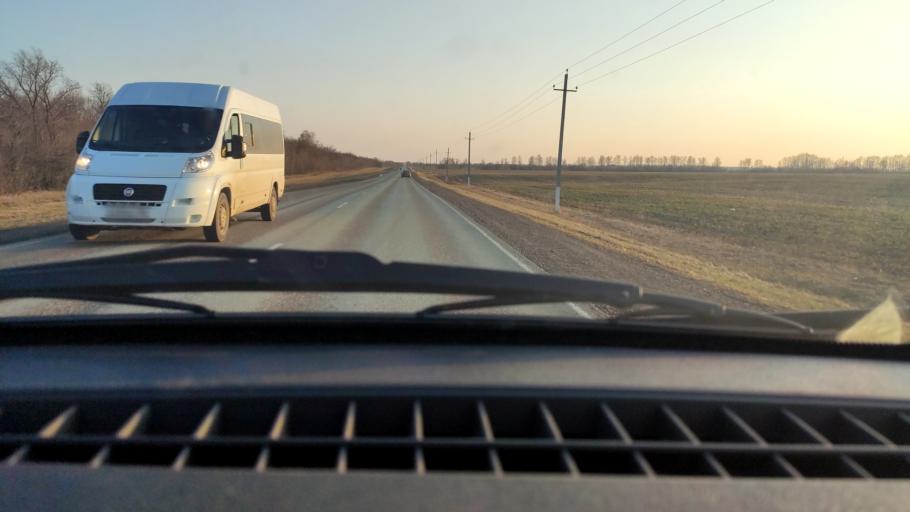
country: RU
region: Bashkortostan
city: Davlekanovo
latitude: 54.3153
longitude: 55.1494
